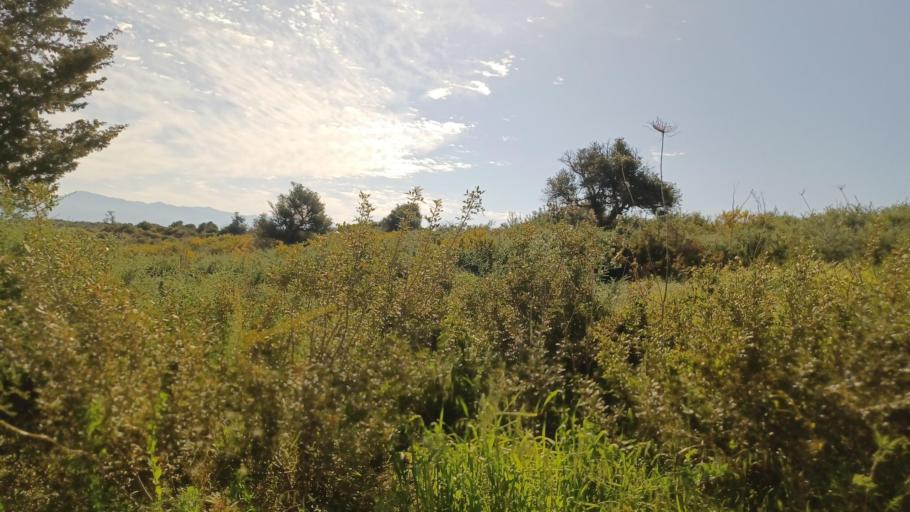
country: CY
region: Pafos
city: Polis
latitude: 35.0390
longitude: 32.3663
